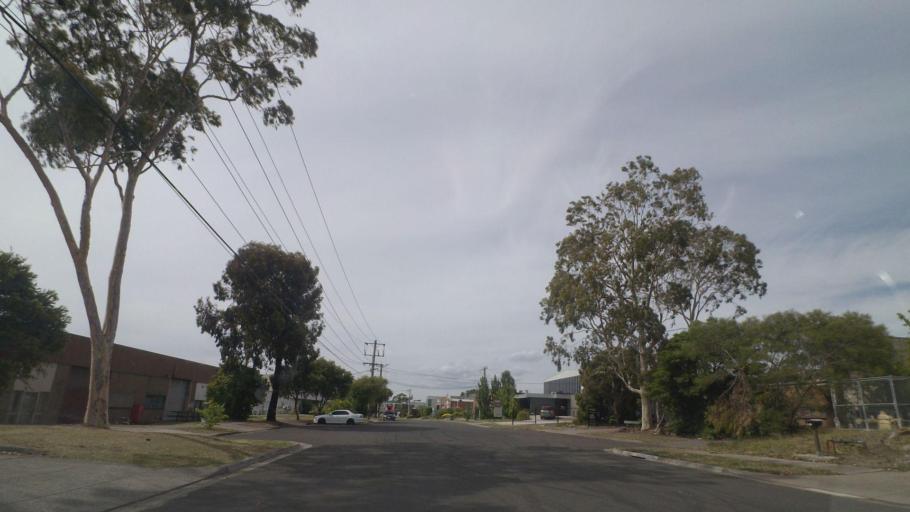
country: AU
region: Victoria
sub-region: Knox
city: Bayswater
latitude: -37.8442
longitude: 145.2815
